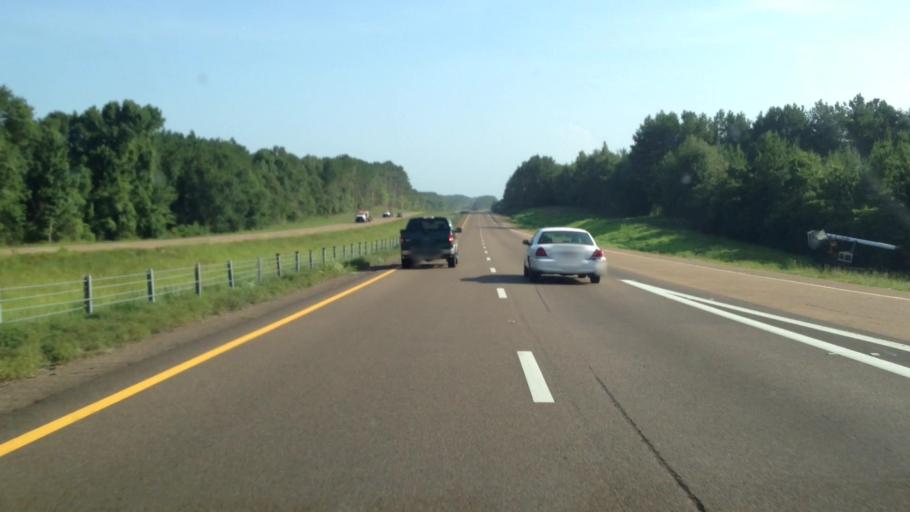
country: US
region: Mississippi
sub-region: Pike County
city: Summit
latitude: 31.4278
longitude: -90.4797
